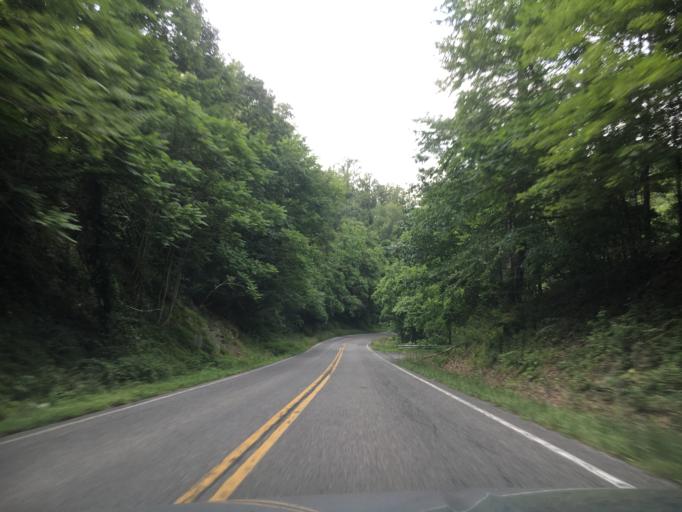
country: US
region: Virginia
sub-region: Roanoke County
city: Narrows
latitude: 37.1742
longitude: -80.0020
